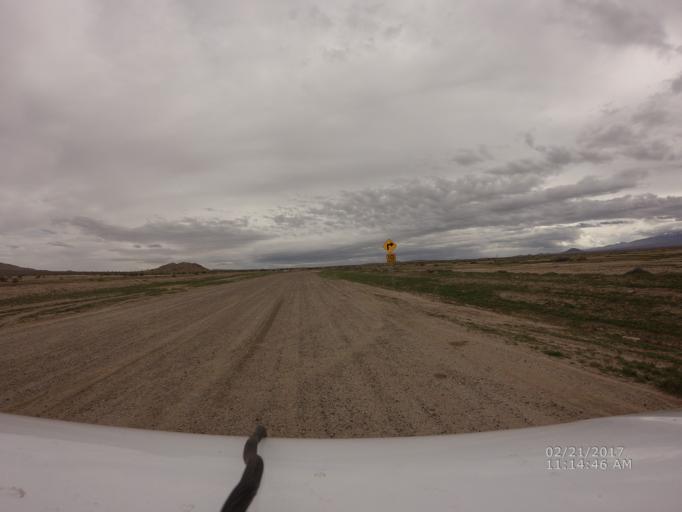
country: US
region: California
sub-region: Los Angeles County
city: Lake Los Angeles
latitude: 34.6459
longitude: -117.8111
